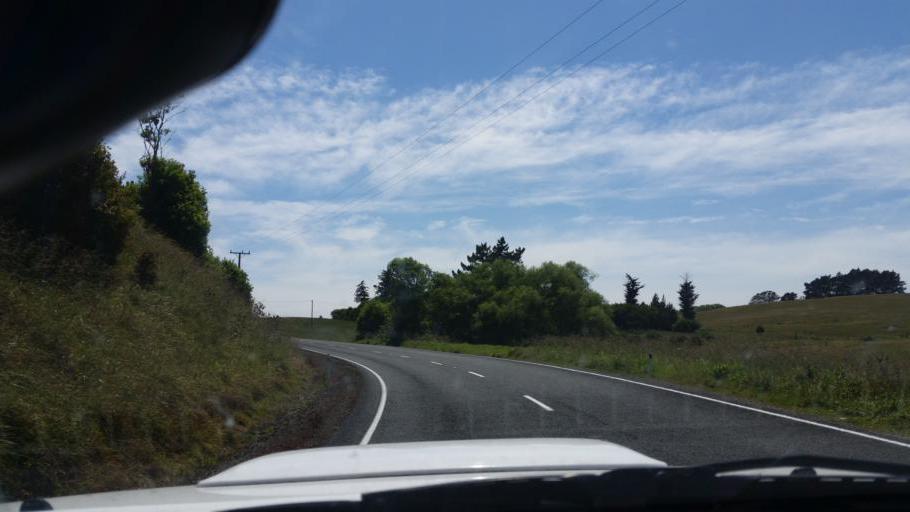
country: NZ
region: Auckland
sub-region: Auckland
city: Wellsford
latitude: -36.1900
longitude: 174.4060
